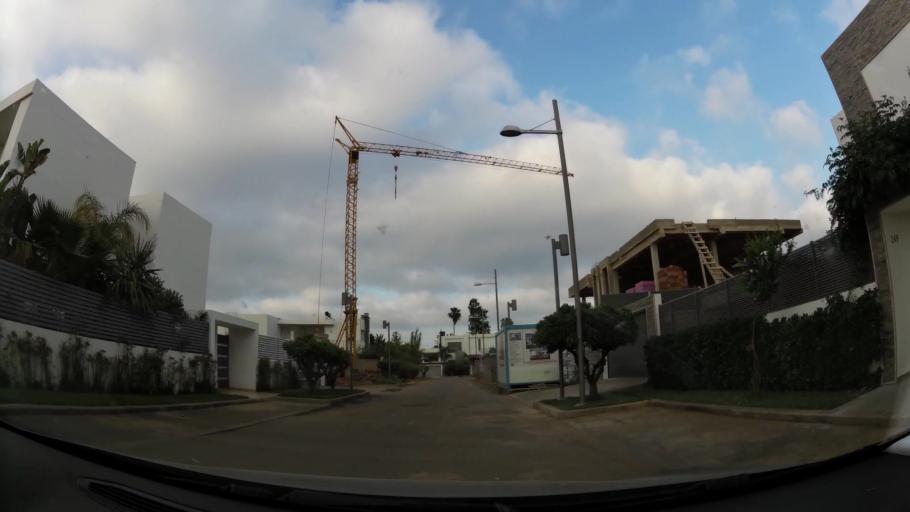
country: MA
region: Rabat-Sale-Zemmour-Zaer
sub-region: Rabat
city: Rabat
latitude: 33.9524
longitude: -6.8373
